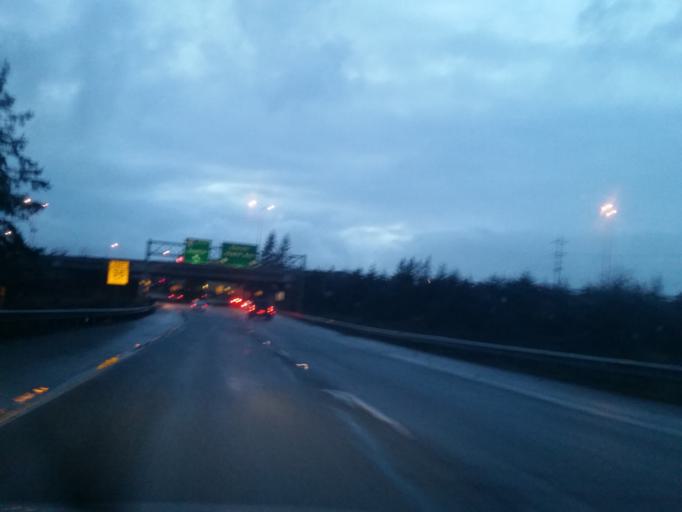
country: US
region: Washington
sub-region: Snohomish County
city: Everett
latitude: 47.9807
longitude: -122.1856
